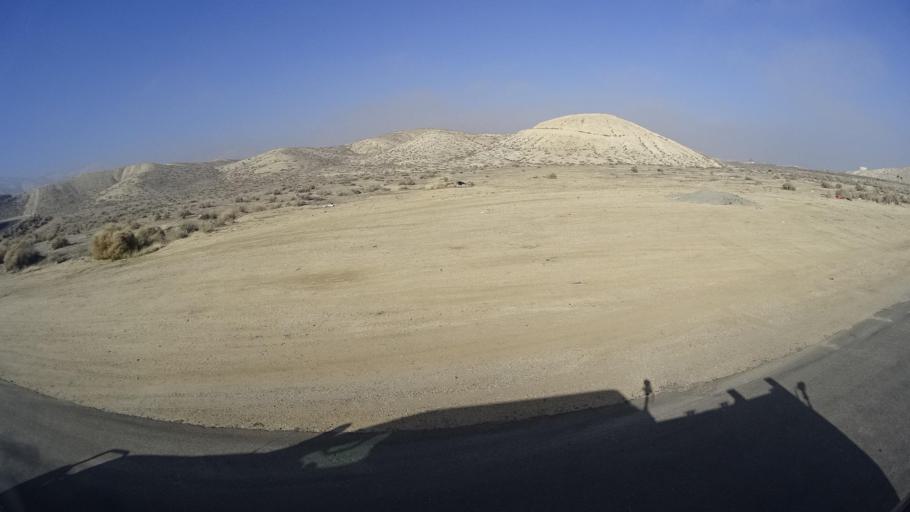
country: US
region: California
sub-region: Kern County
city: Maricopa
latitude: 35.0395
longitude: -119.4237
